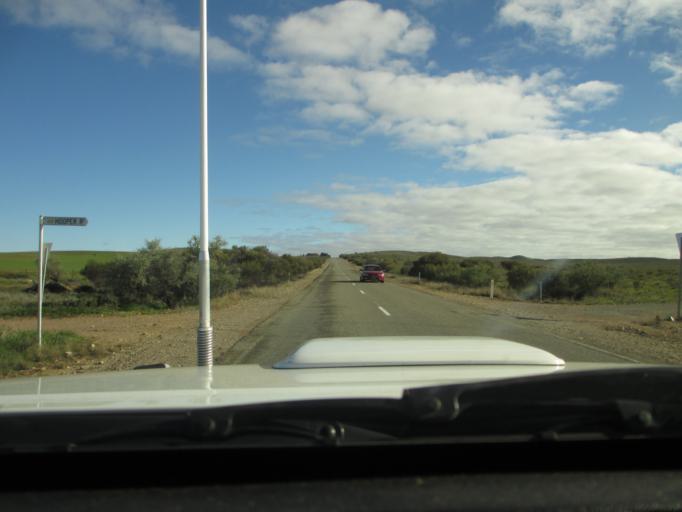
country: AU
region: South Australia
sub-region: Peterborough
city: Peterborough
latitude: -32.6264
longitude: 138.5855
